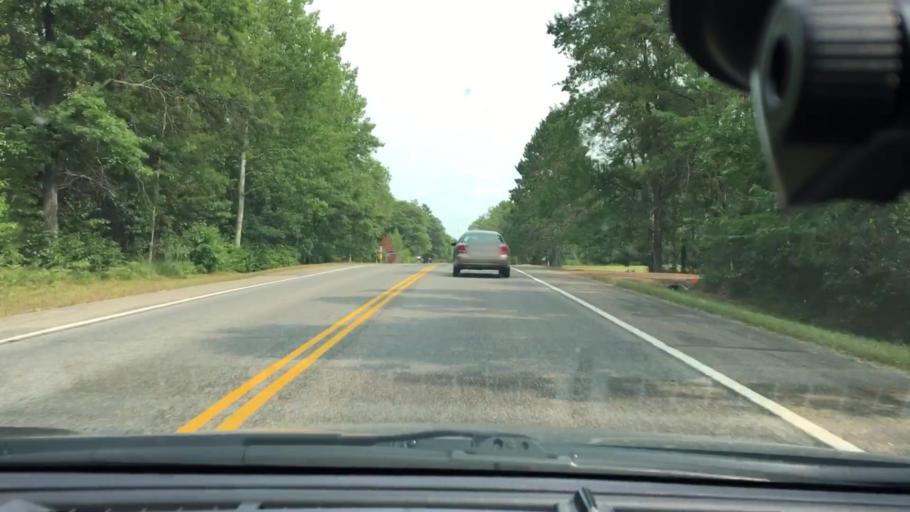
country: US
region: Minnesota
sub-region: Cass County
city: East Gull Lake
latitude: 46.4128
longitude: -94.3151
